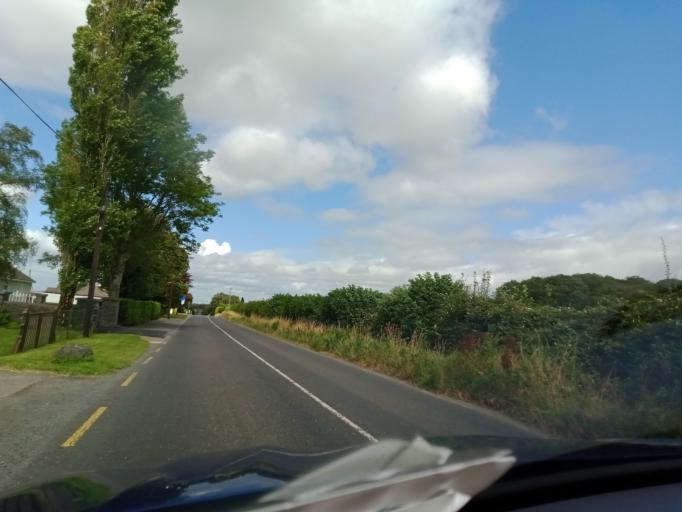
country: IE
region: Leinster
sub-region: Laois
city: Portlaoise
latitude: 52.9683
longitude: -7.2950
